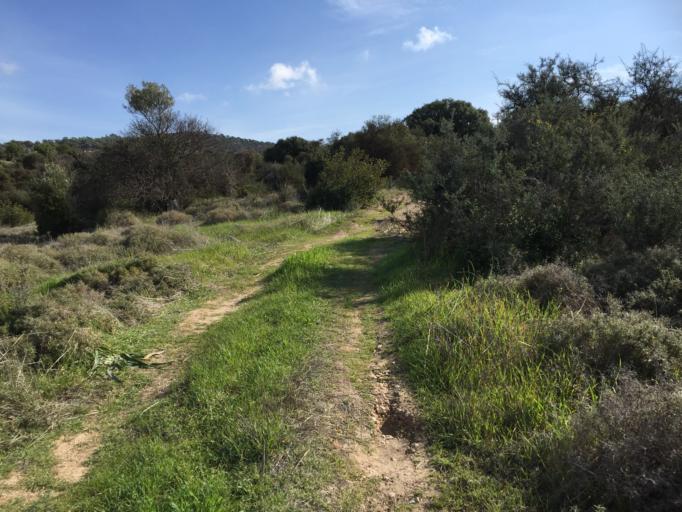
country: CY
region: Limassol
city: Mouttagiaka
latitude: 34.7465
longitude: 33.1128
